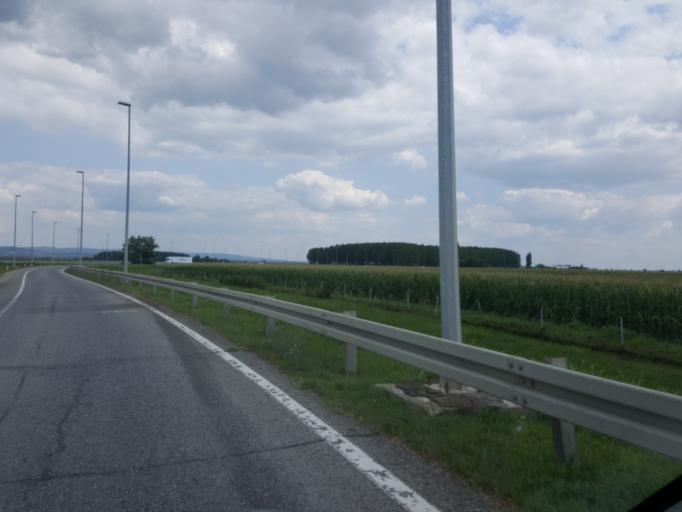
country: RS
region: Autonomna Pokrajina Vojvodina
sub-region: Sremski Okrug
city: Sremska Mitrovica
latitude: 44.9965
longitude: 19.6509
